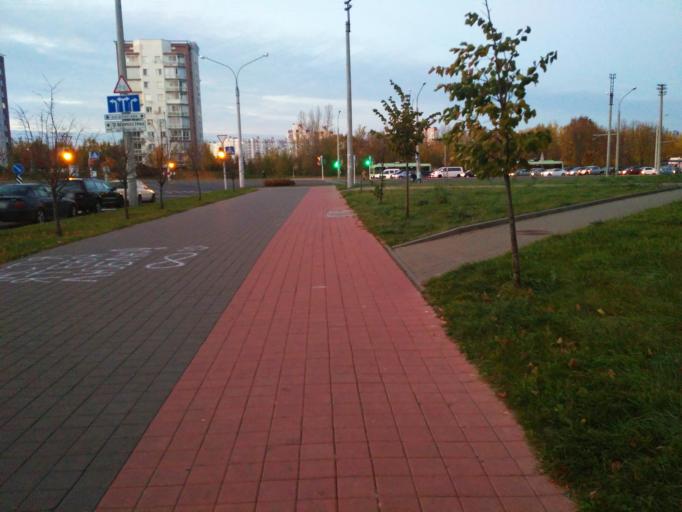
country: BY
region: Minsk
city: Novoye Medvezhino
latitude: 53.8713
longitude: 27.4864
